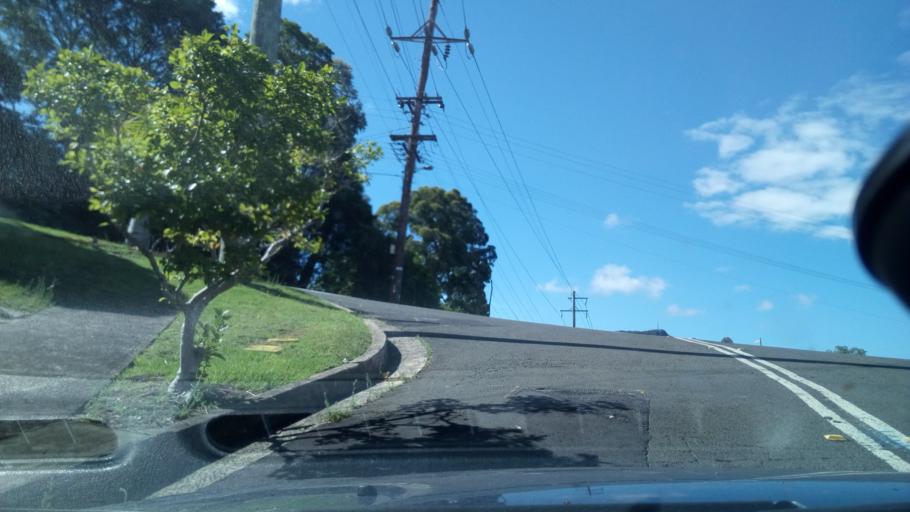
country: AU
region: New South Wales
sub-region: Wollongong
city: Mount Ousley
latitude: -34.3944
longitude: 150.8701
